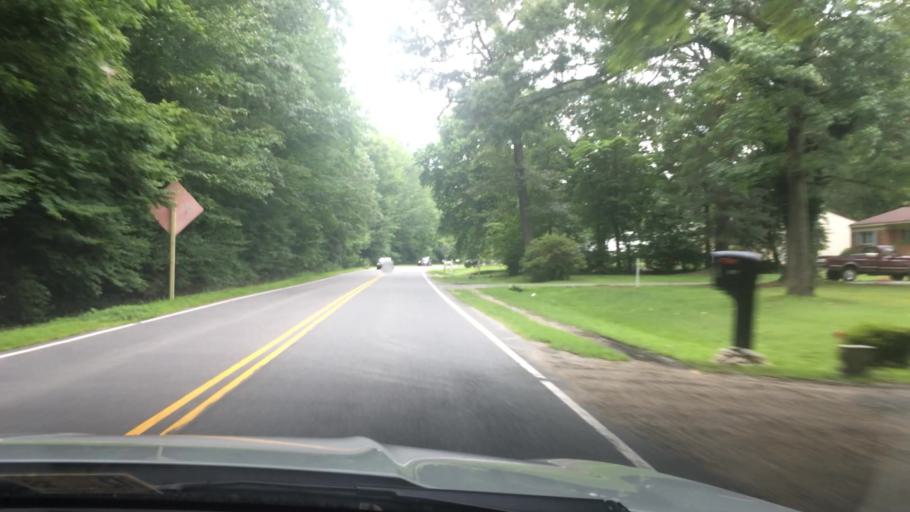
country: US
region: Virginia
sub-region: York County
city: Yorktown
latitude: 37.2279
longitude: -76.5246
